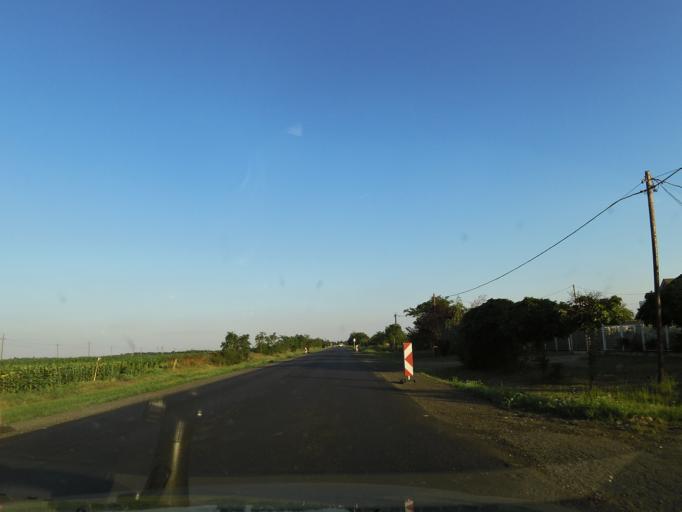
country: HU
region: Csongrad
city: Szentes
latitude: 46.6167
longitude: 20.2849
